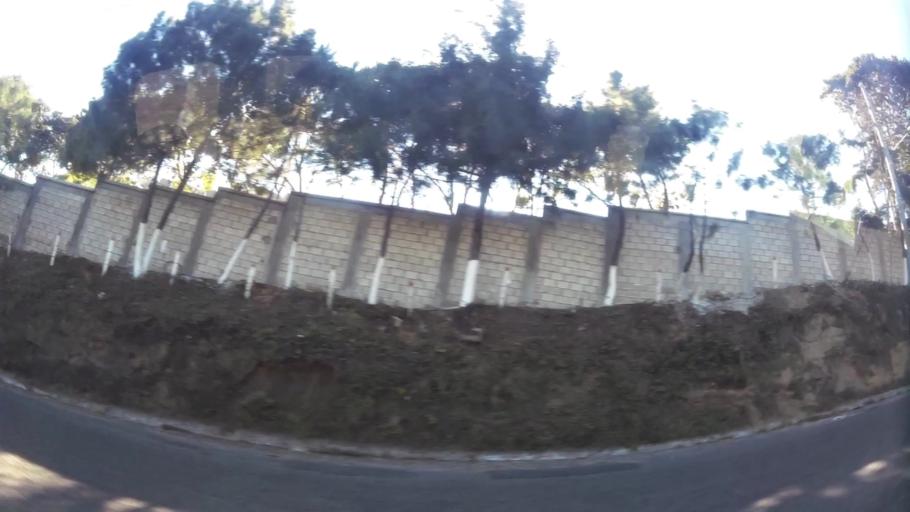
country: GT
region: Sacatepequez
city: Magdalena Milpas Altas
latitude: 14.5599
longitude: -90.6364
